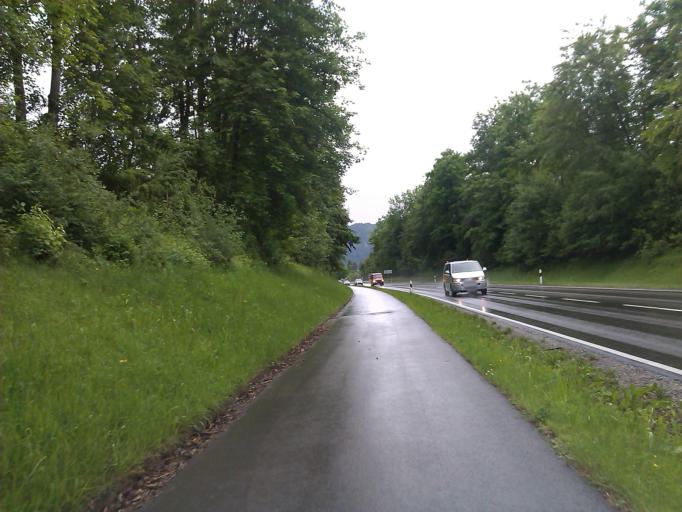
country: DE
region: Bavaria
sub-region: Swabia
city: Fuessen
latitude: 47.5901
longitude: 10.7077
